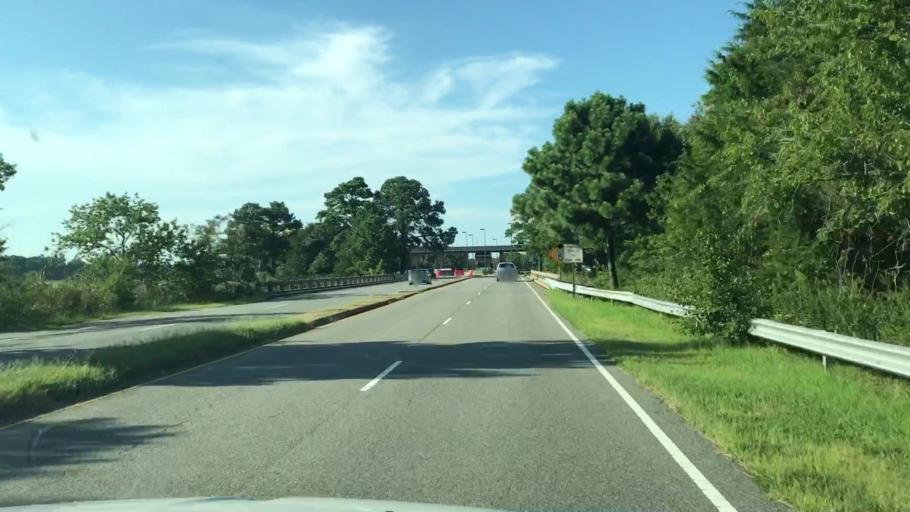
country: US
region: Virginia
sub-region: City of Hampton
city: Hampton
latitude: 37.0632
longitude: -76.3659
